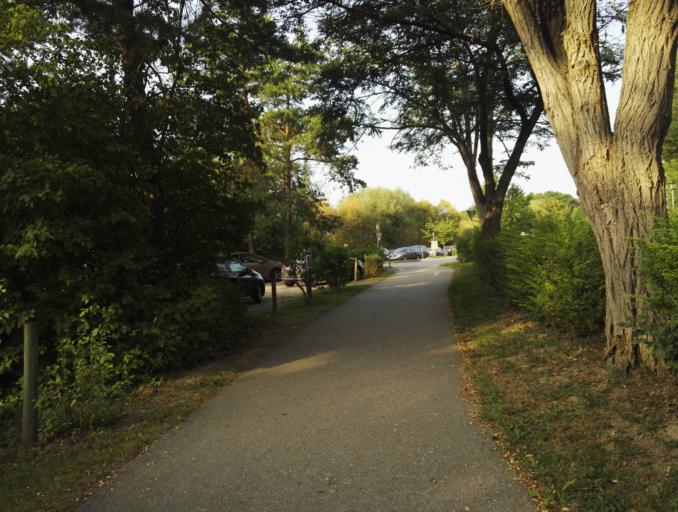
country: AT
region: Styria
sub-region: Politischer Bezirk Hartberg-Fuerstenfeld
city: Loipersdorf bei Fuerstenfeld
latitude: 46.9862
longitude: 16.1103
